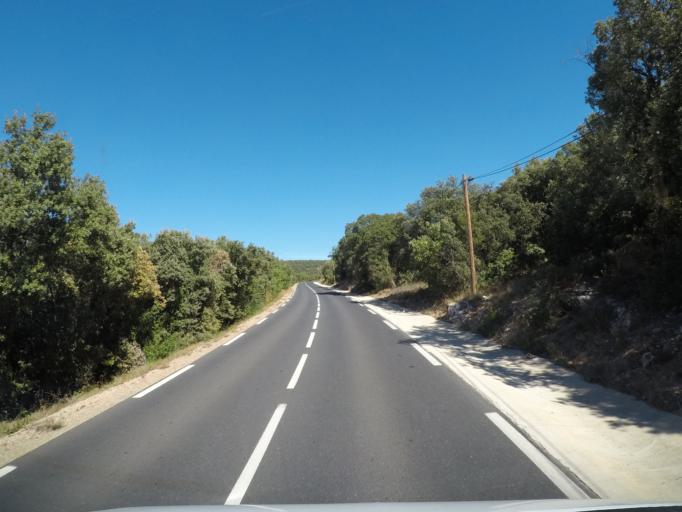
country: FR
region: Languedoc-Roussillon
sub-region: Departement de l'Herault
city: Aniane
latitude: 43.7187
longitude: 3.6235
